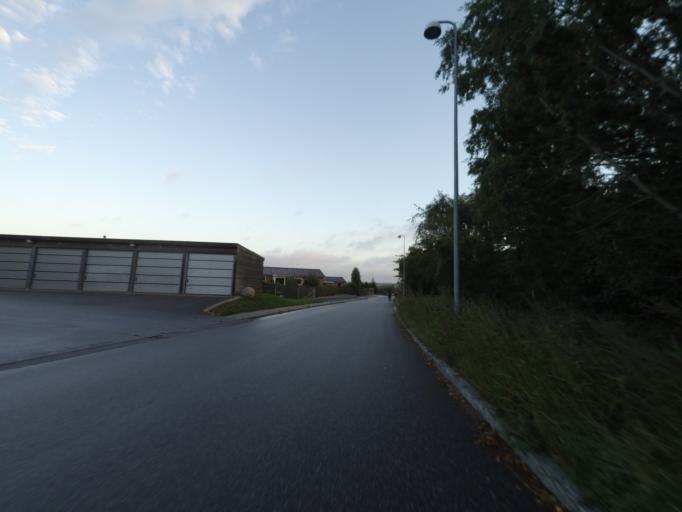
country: DK
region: Central Jutland
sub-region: Arhus Kommune
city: Arhus
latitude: 56.1362
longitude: 10.1728
